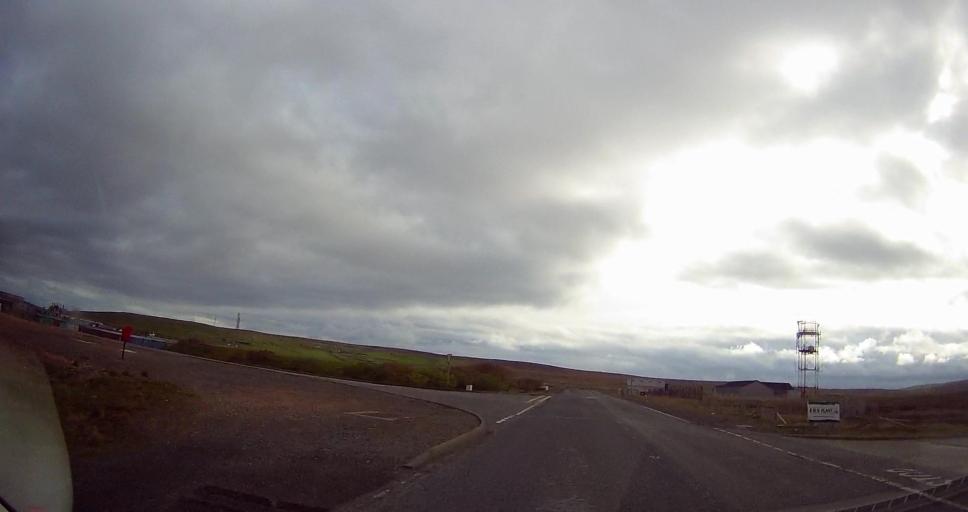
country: GB
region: Scotland
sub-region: Shetland Islands
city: Lerwick
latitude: 60.4392
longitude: -1.2743
